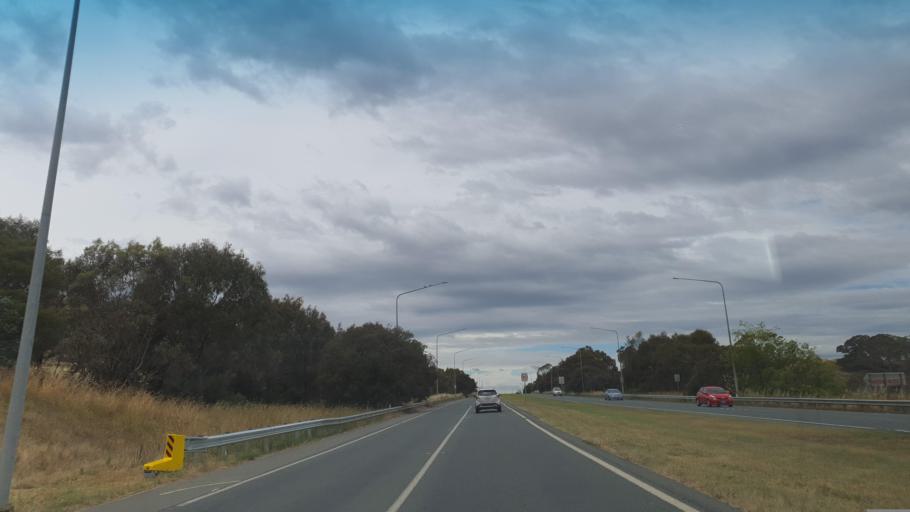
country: AU
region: Australian Capital Territory
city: Macquarie
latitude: -35.2712
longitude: 149.0565
